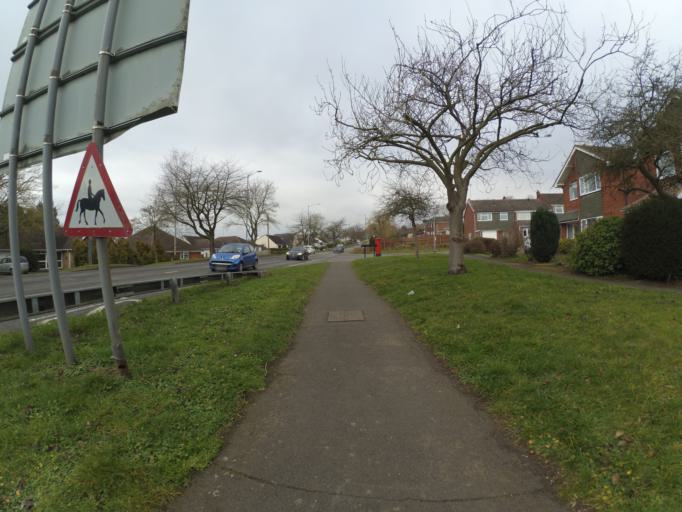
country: GB
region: England
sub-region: Warwickshire
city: Rugby
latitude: 52.3562
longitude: -1.2009
